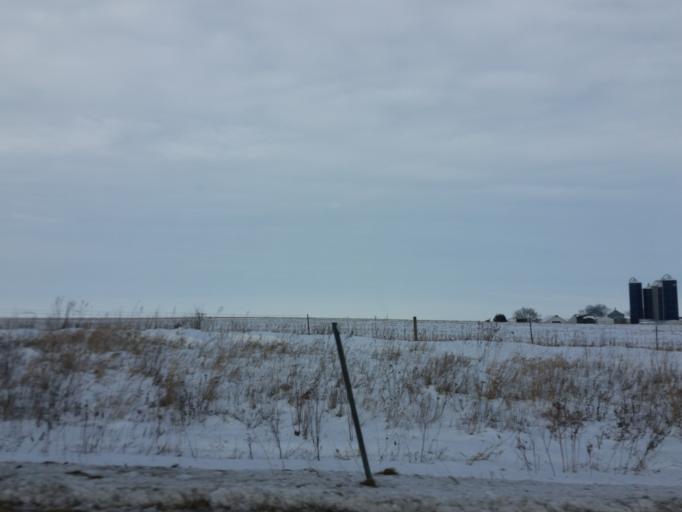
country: US
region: Iowa
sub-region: Delaware County
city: Manchester
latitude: 42.4644
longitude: -91.5816
